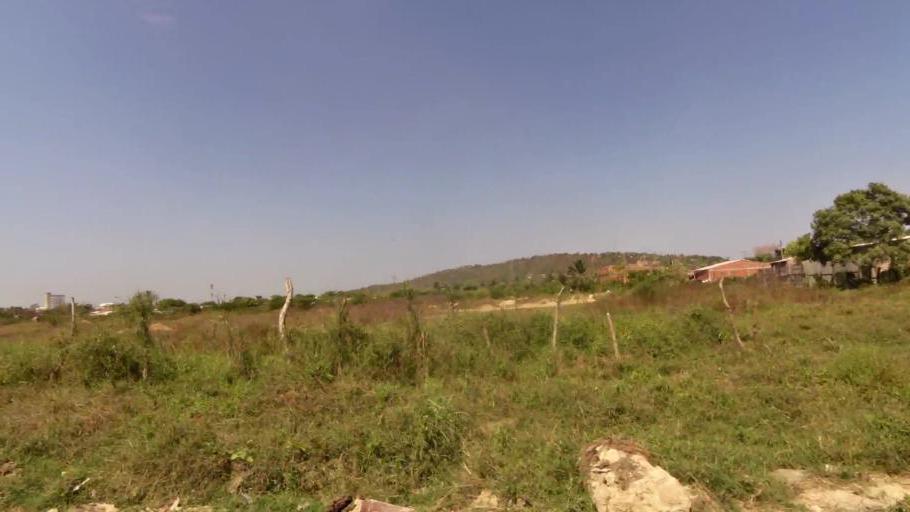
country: CO
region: Bolivar
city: Cartagena
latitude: 10.3528
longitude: -75.4853
